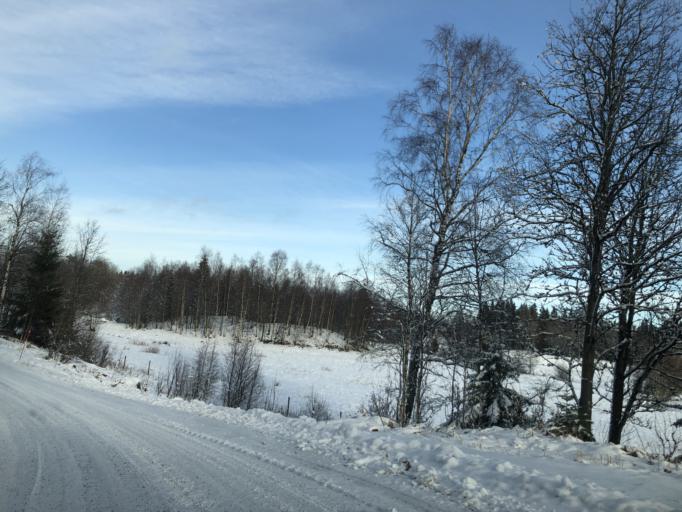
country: SE
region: Vaestra Goetaland
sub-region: Ulricehamns Kommun
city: Ulricehamn
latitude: 57.7683
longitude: 13.5214
